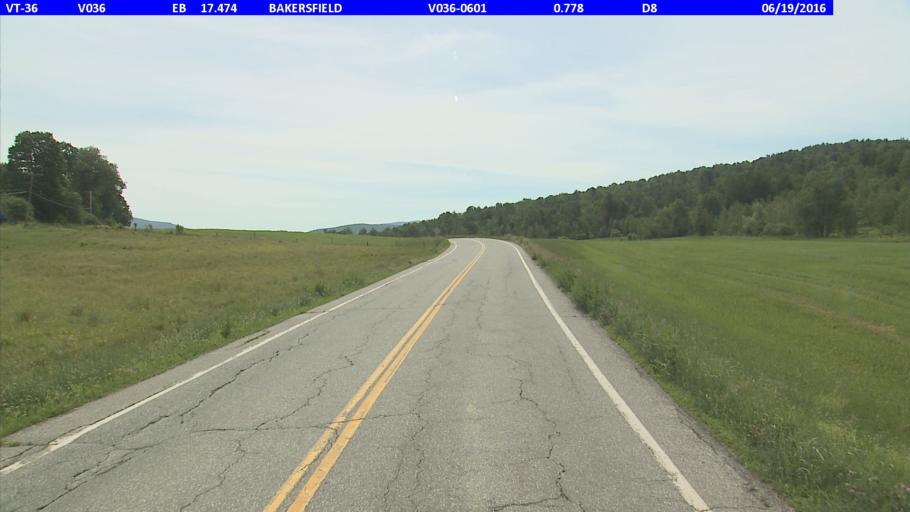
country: US
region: Vermont
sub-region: Franklin County
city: Enosburg Falls
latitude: 44.7840
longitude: -72.8344
